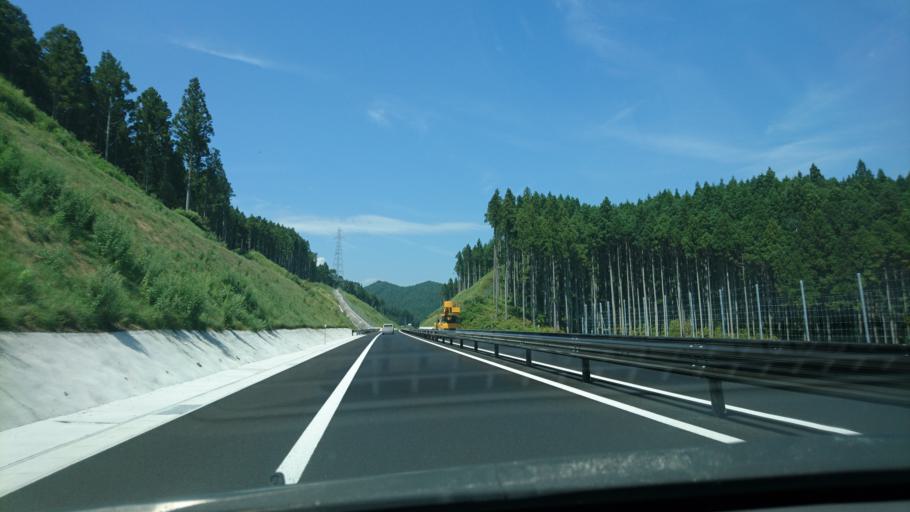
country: JP
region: Iwate
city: Ofunato
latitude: 39.0089
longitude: 141.6106
